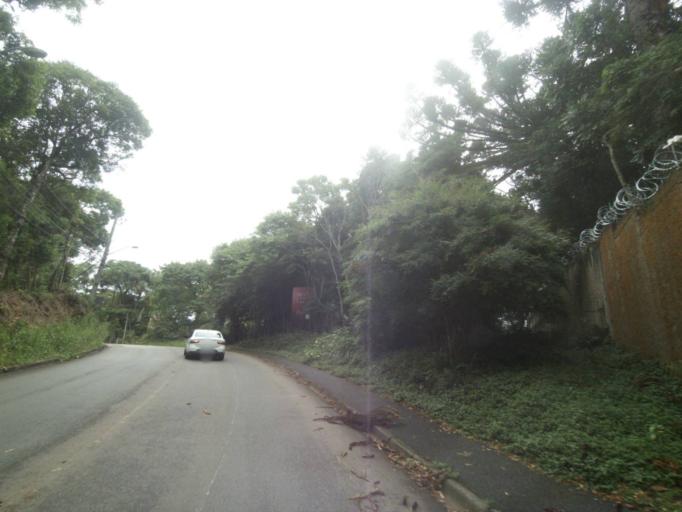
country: BR
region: Parana
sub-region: Curitiba
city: Curitiba
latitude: -25.4536
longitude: -49.3333
